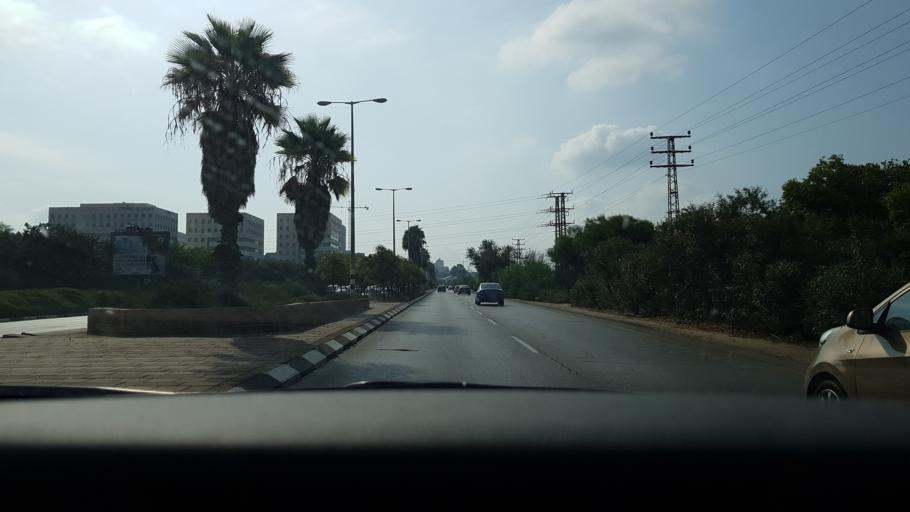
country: IL
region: Central District
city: Ness Ziona
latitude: 31.9170
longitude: 34.8000
